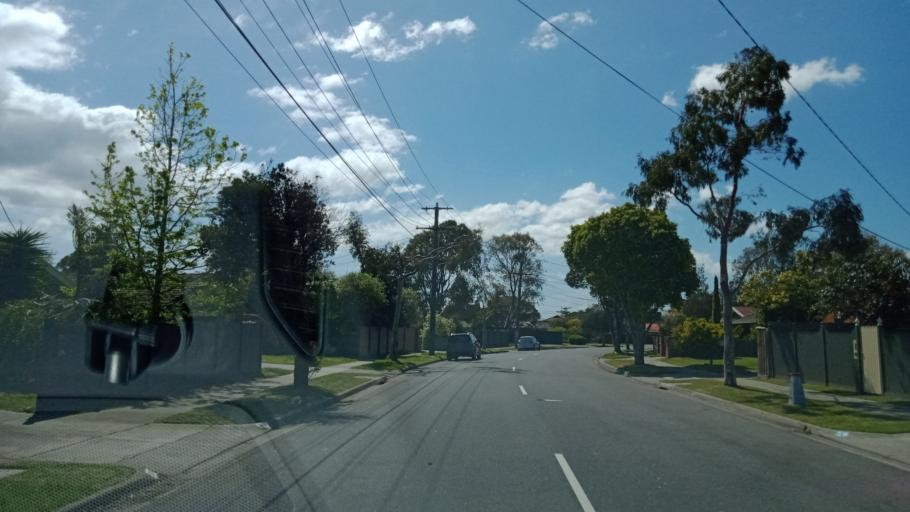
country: AU
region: Victoria
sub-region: Kingston
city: Chelsea Heights
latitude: -38.0355
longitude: 145.1313
